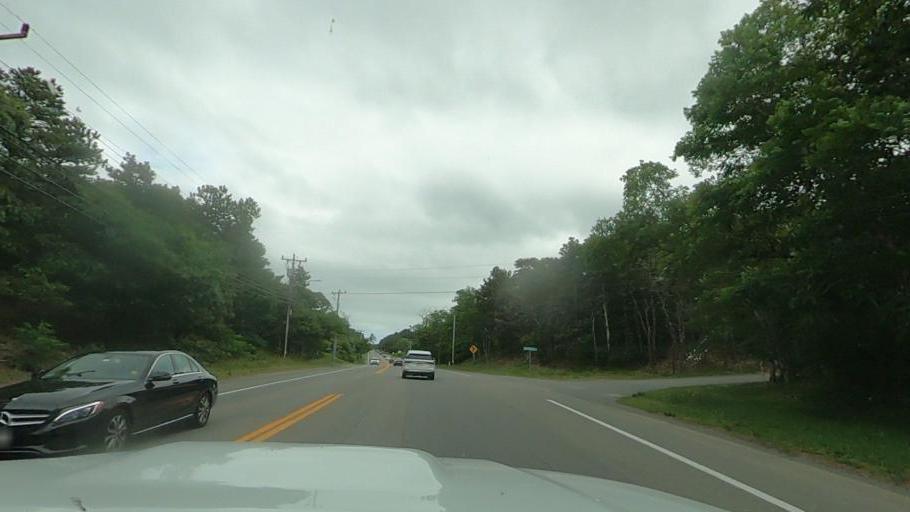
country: US
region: Massachusetts
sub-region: Barnstable County
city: Wellfleet
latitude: 41.9314
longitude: -70.0183
